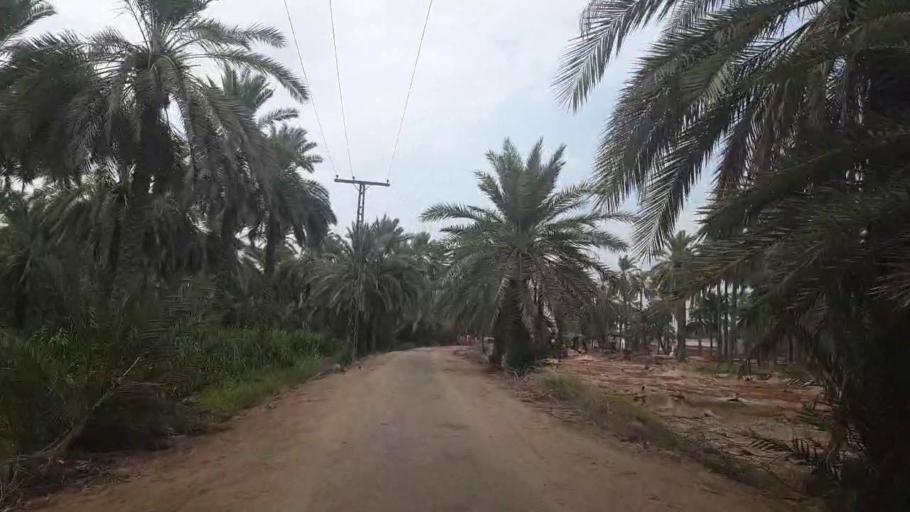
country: PK
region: Sindh
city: Sukkur
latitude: 27.6300
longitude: 68.7896
